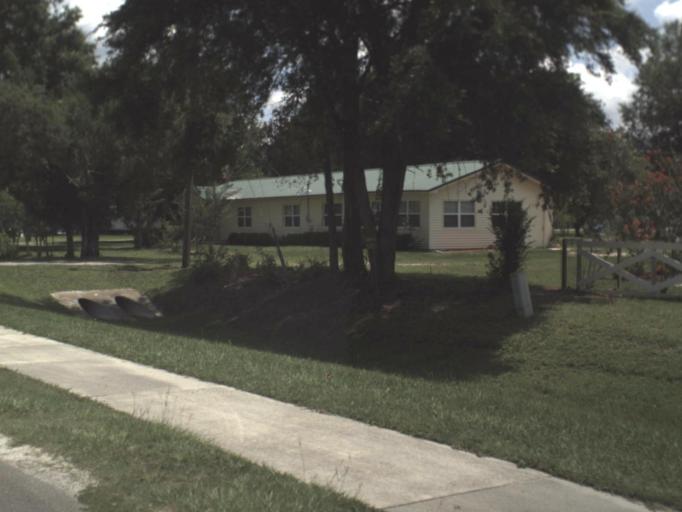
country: US
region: Florida
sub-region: Union County
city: Lake Butler
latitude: 30.0127
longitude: -82.3445
